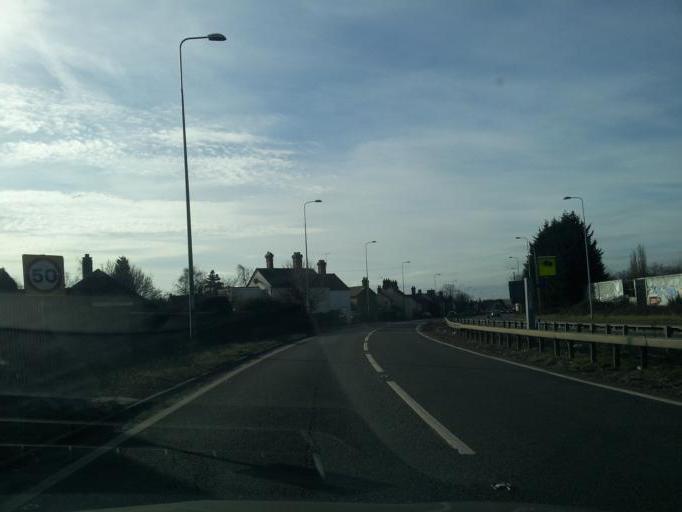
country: GB
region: England
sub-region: Central Bedfordshire
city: Sandy
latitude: 52.1374
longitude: -0.2982
